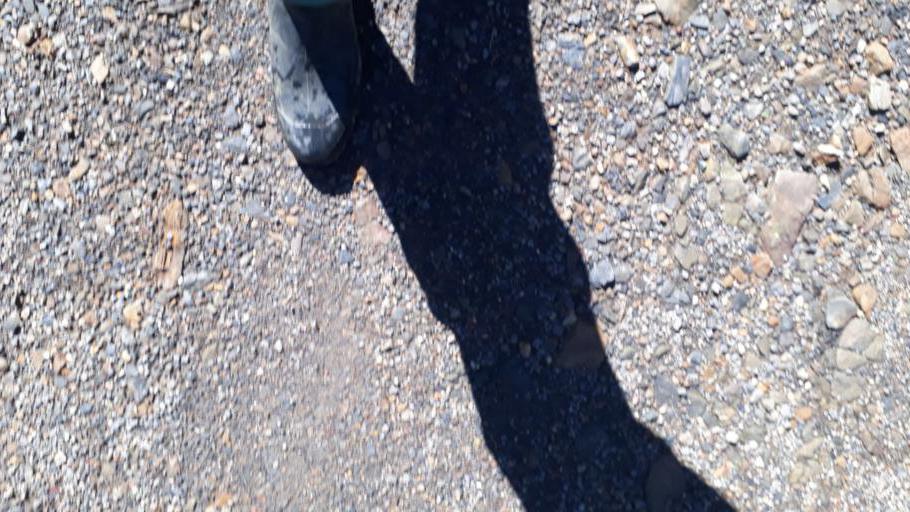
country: CO
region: Casanare
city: Nunchia
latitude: 5.6525
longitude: -72.4228
